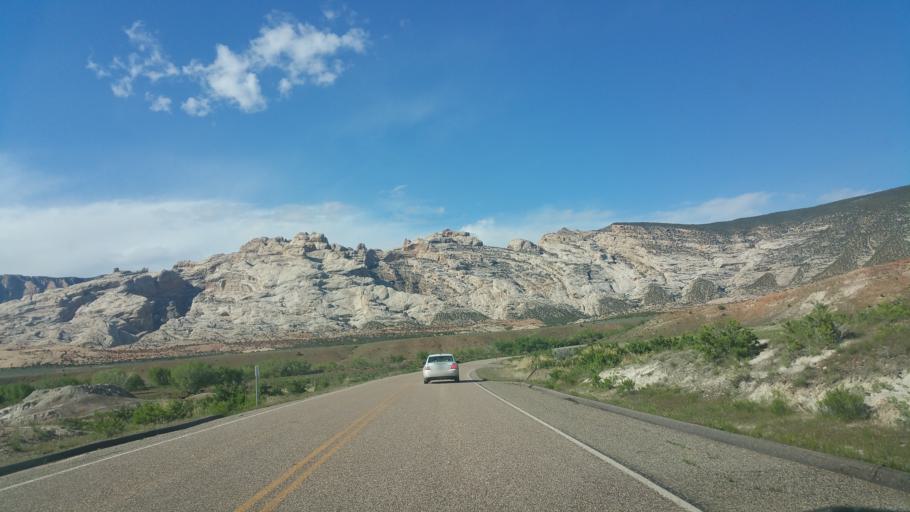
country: US
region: Utah
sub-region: Uintah County
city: Naples
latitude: 40.4187
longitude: -109.2273
